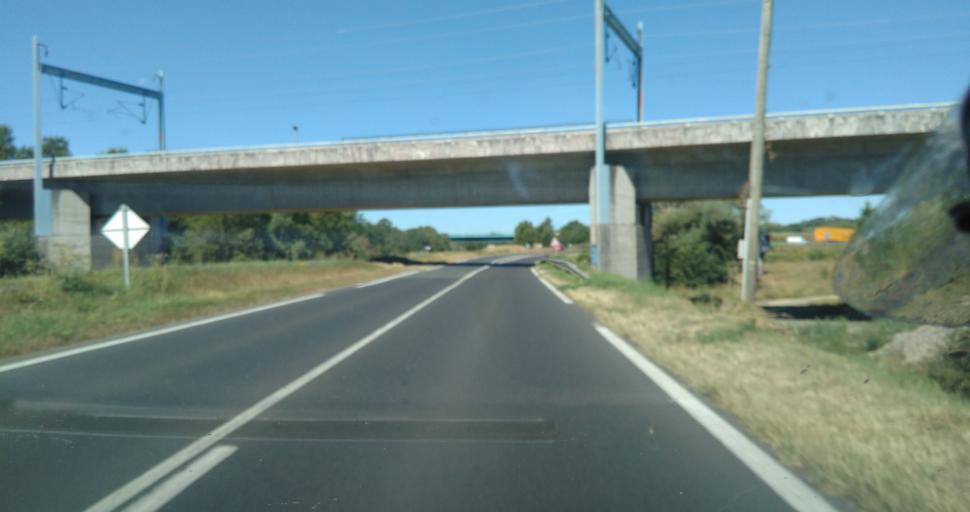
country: FR
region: Centre
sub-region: Departement d'Indre-et-Loire
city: Vouvray
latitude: 47.4027
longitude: 0.8094
